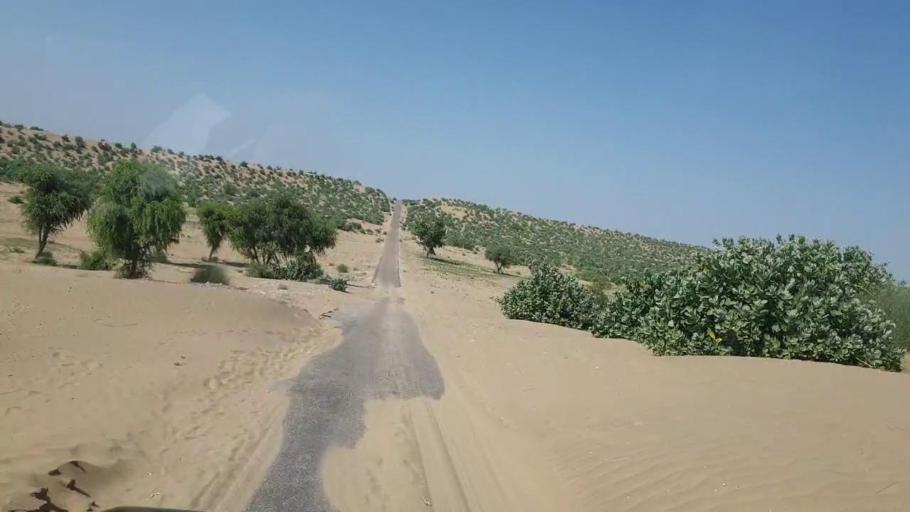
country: PK
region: Sindh
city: Chor
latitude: 25.6159
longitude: 70.3178
